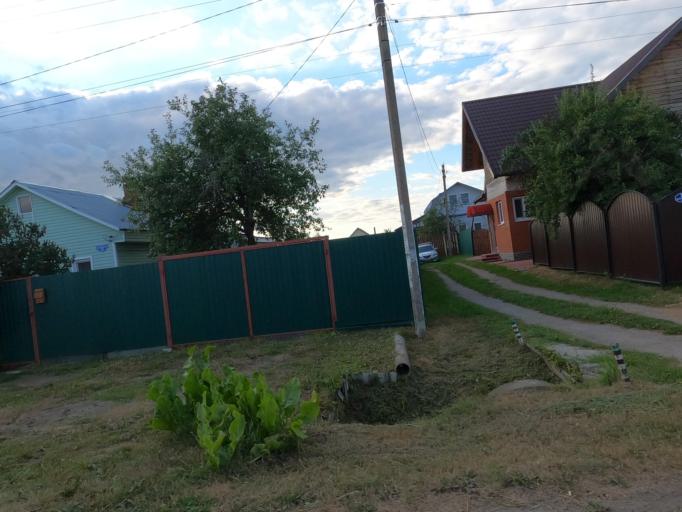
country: RU
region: Moskovskaya
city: Ashitkovo
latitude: 55.4228
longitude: 38.5882
